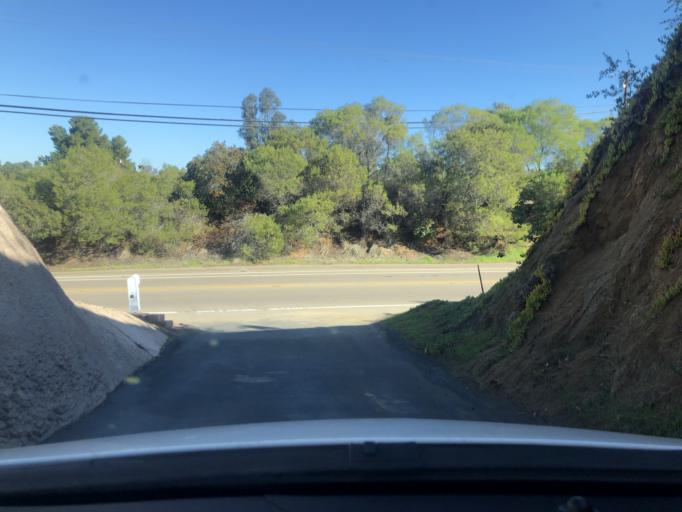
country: US
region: California
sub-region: San Diego County
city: Rancho San Diego
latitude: 32.7723
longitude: -116.9409
